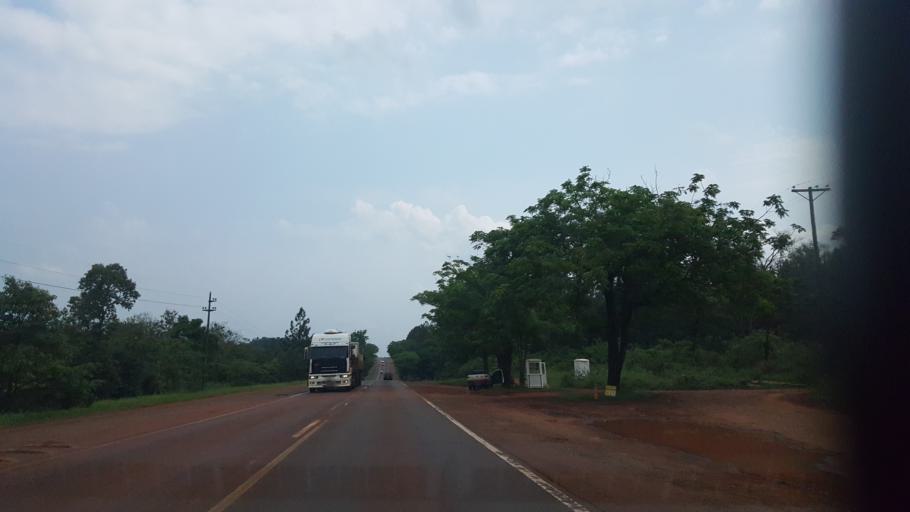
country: AR
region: Misiones
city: Jardin America
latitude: -27.0638
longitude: -55.2636
